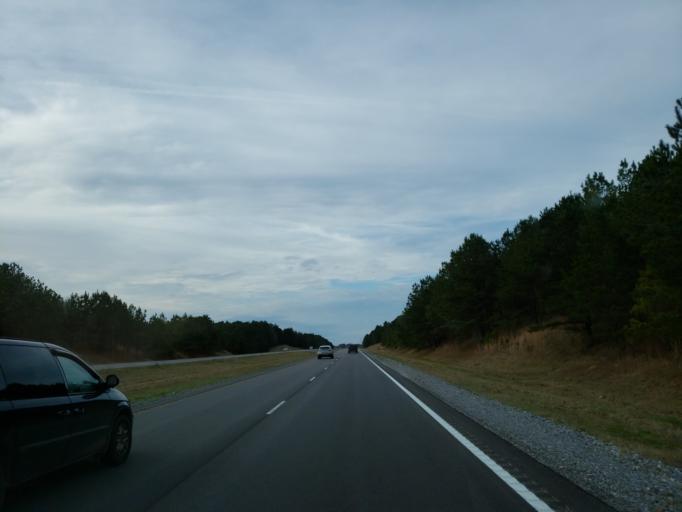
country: US
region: Mississippi
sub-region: Clarke County
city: Quitman
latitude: 32.0839
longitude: -88.6943
